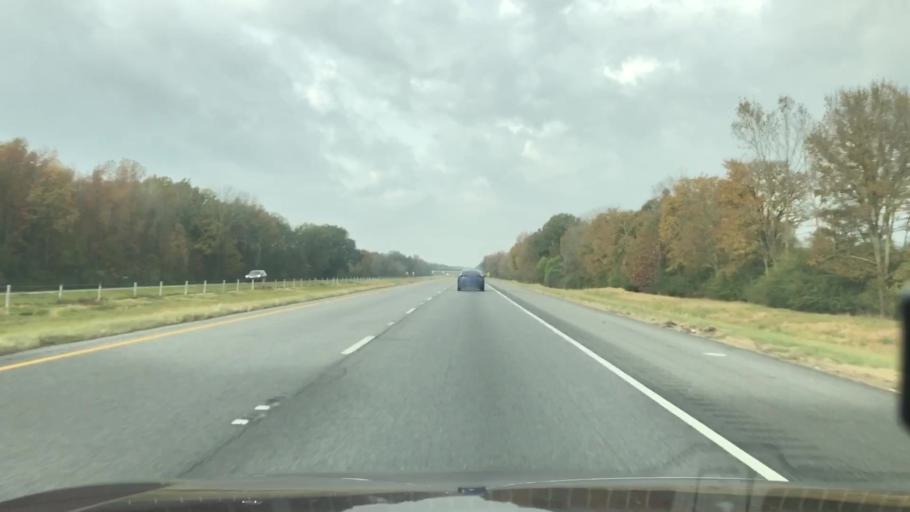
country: US
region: Louisiana
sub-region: Richland Parish
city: Delhi
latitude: 32.4452
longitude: -91.5145
